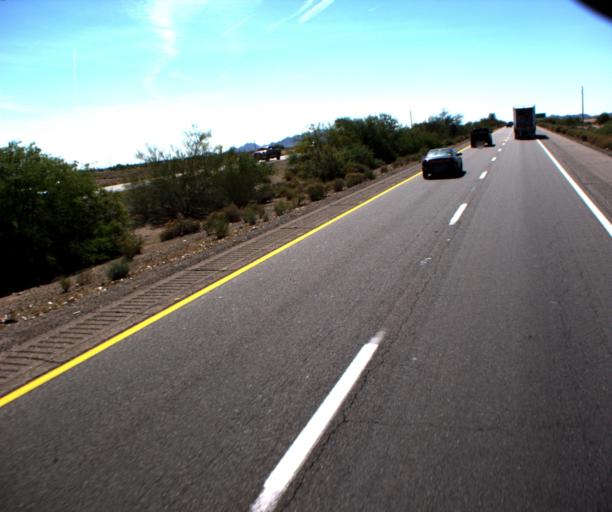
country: US
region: Arizona
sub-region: Pinal County
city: Casa Blanca
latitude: 33.1056
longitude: -111.8327
